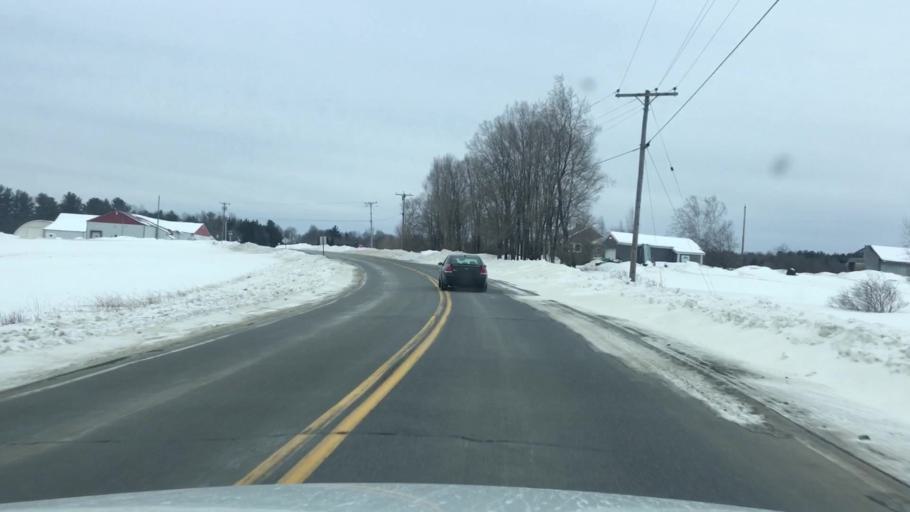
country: US
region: Maine
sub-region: Penobscot County
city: Garland
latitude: 44.9905
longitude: -69.0876
